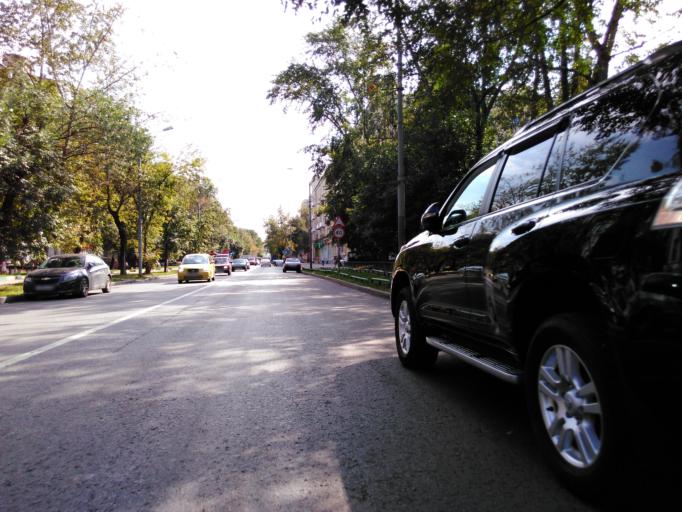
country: RU
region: Moskovskaya
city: Bol'shaya Setun'
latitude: 55.7226
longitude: 37.4008
